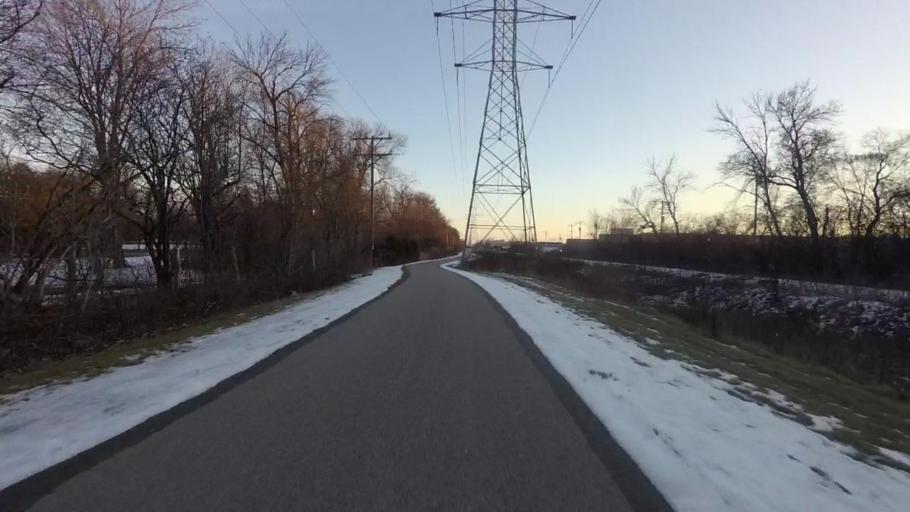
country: US
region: Wisconsin
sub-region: Milwaukee County
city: Brown Deer
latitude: 43.1527
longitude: -87.9563
